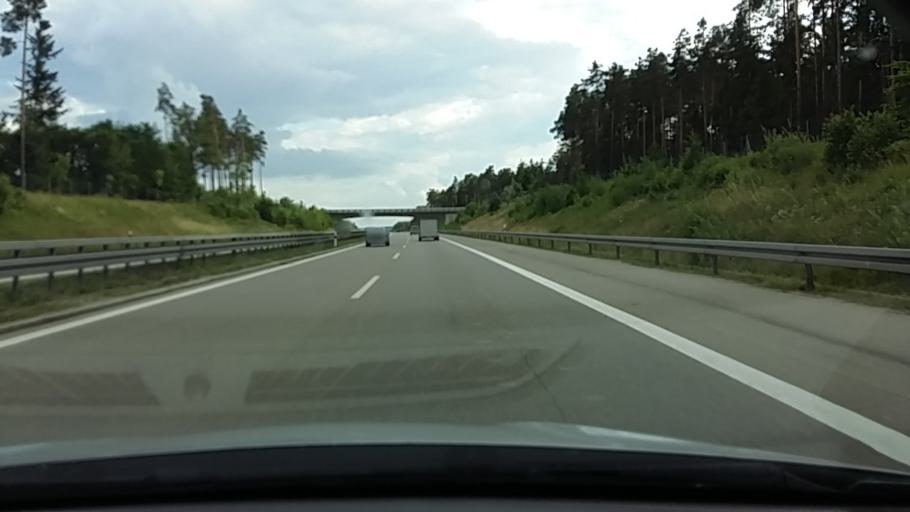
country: DE
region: Bavaria
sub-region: Upper Palatinate
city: Ebermannsdorf
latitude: 49.4191
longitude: 11.9965
